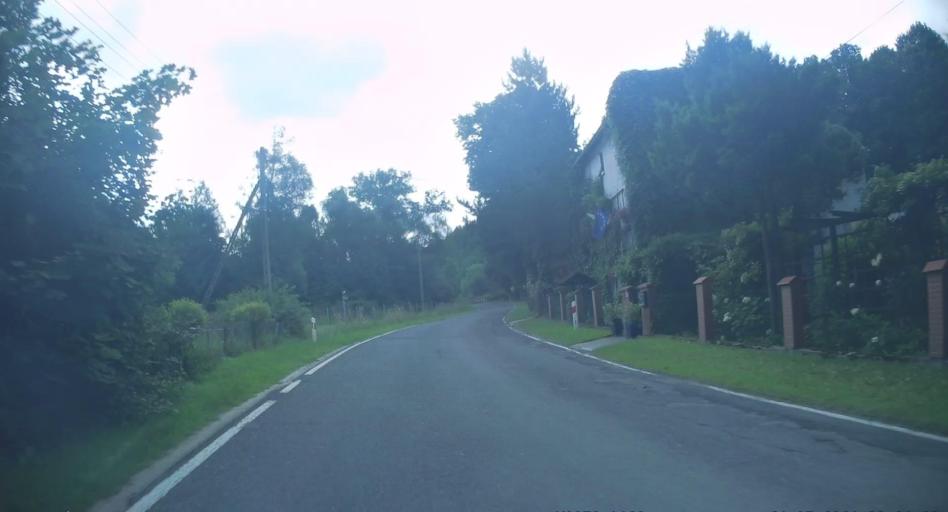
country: PL
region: Lower Silesian Voivodeship
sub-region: Powiat walbrzyski
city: Walim
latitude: 50.7183
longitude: 16.4204
